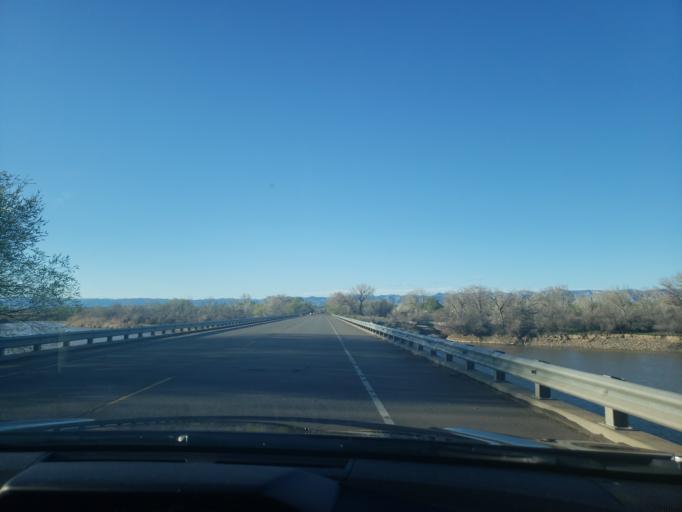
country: US
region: Colorado
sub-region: Mesa County
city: Fruita
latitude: 39.1408
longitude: -108.7383
